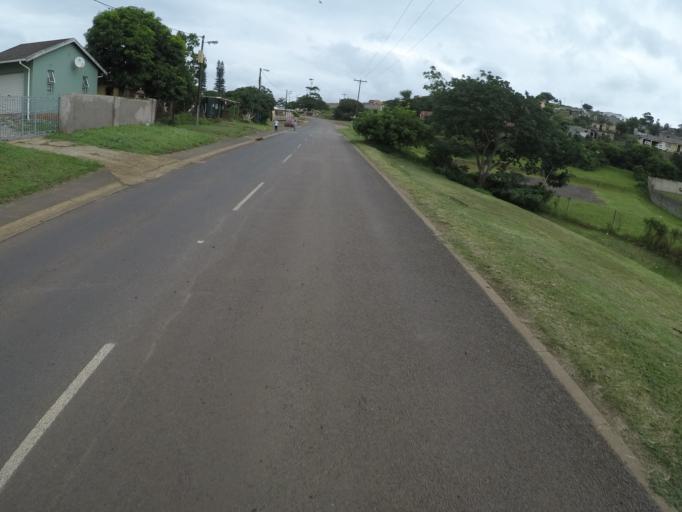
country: ZA
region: KwaZulu-Natal
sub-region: uThungulu District Municipality
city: Empangeni
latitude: -28.7728
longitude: 31.8573
